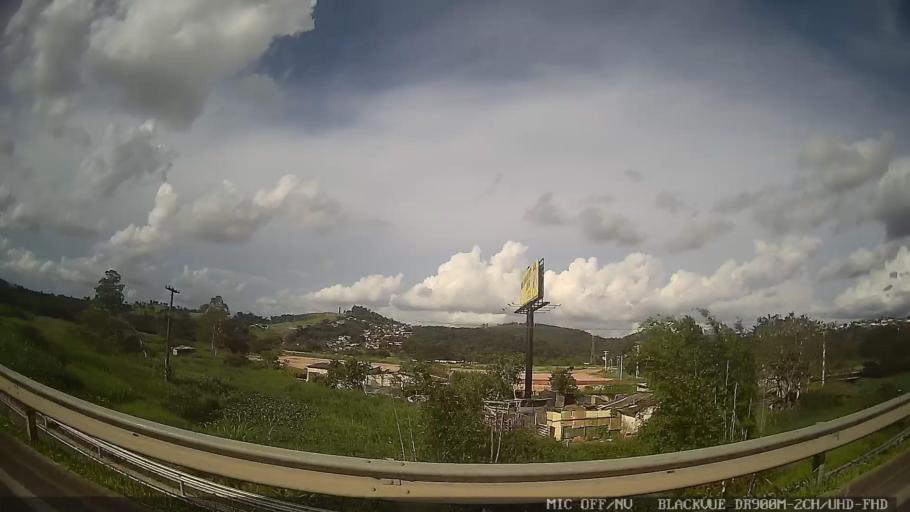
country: BR
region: Sao Paulo
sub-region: Bom Jesus Dos Perdoes
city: Bom Jesus dos Perdoes
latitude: -23.1324
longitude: -46.4647
